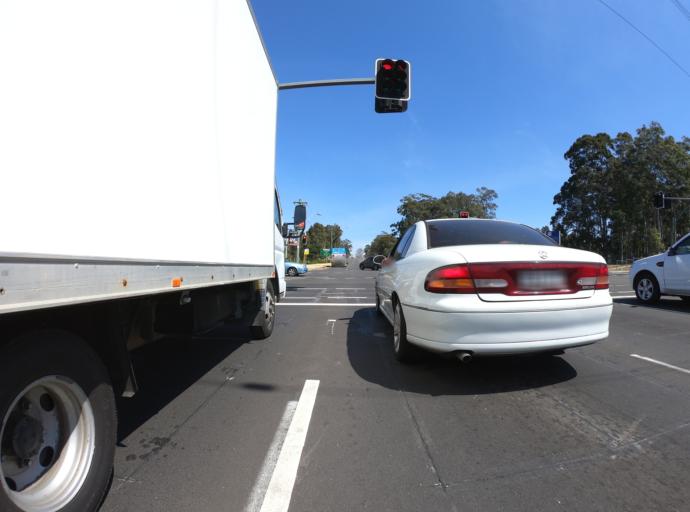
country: AU
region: New South Wales
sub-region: The Hills Shire
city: Castle Hill
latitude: -33.7249
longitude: 150.9772
